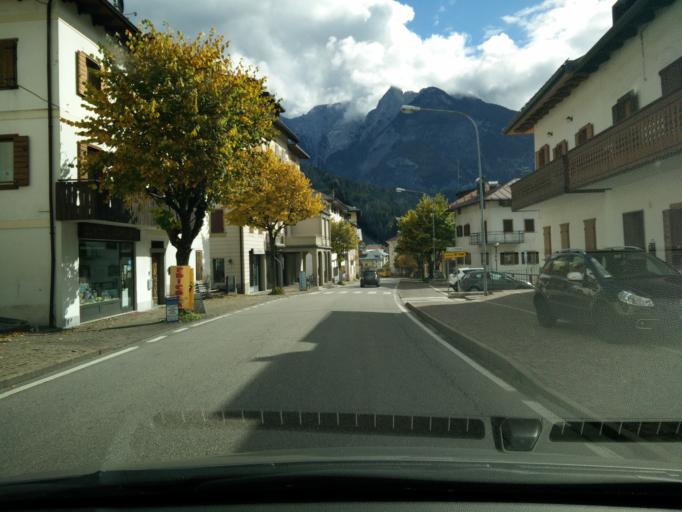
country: IT
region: Veneto
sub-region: Provincia di Belluno
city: Auronzo
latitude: 46.5465
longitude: 12.4546
